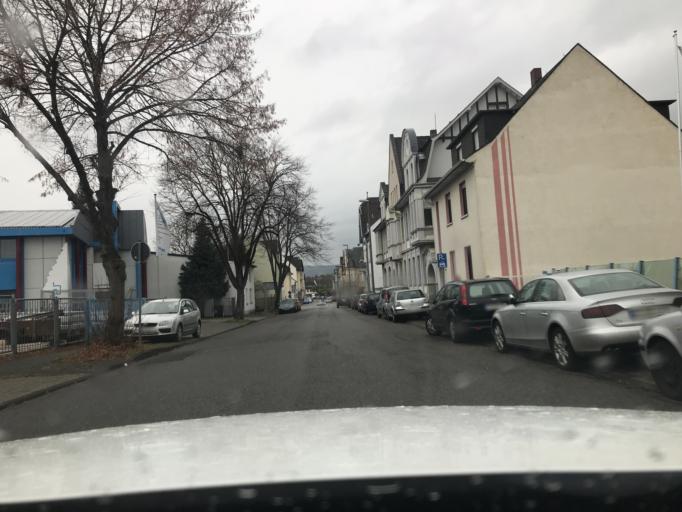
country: DE
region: Rheinland-Pfalz
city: Neuwied
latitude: 50.4325
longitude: 7.4696
